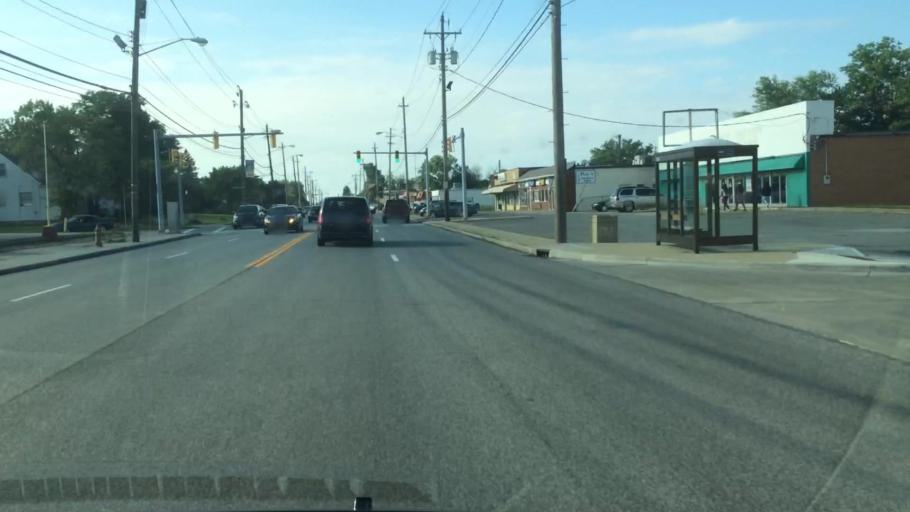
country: US
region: Ohio
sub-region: Cuyahoga County
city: Garfield Heights
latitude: 41.4057
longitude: -81.5978
